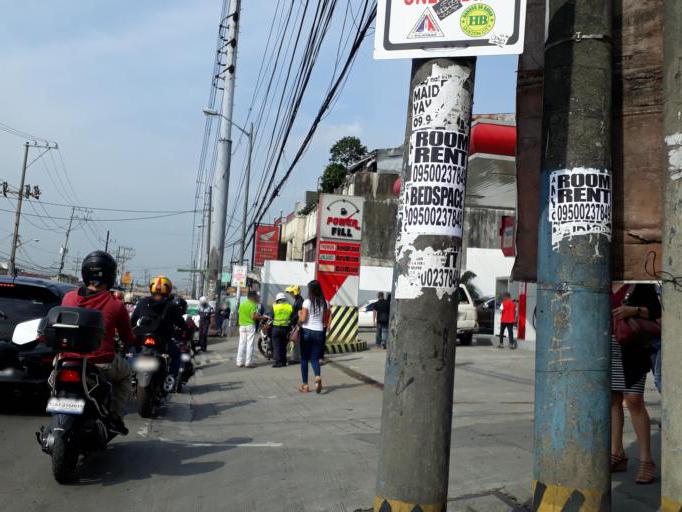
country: PH
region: Calabarzon
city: Bagong Pagasa
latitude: 14.6924
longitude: 121.0294
